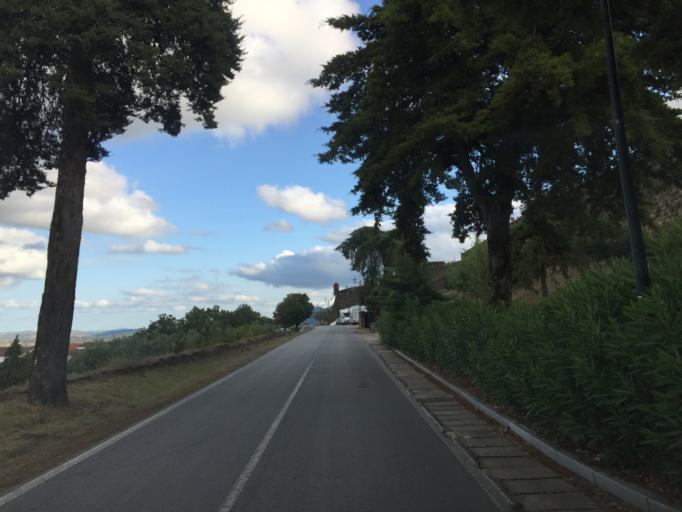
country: PT
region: Portalegre
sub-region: Marvao
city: Marvao
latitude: 39.3952
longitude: -7.3759
